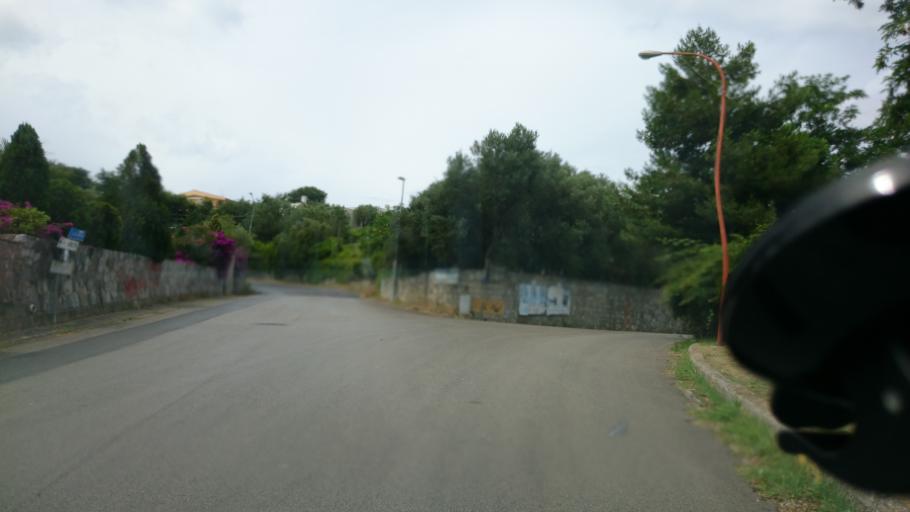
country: IT
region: Campania
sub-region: Provincia di Salerno
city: Palinuro
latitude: 40.0309
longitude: 15.2898
